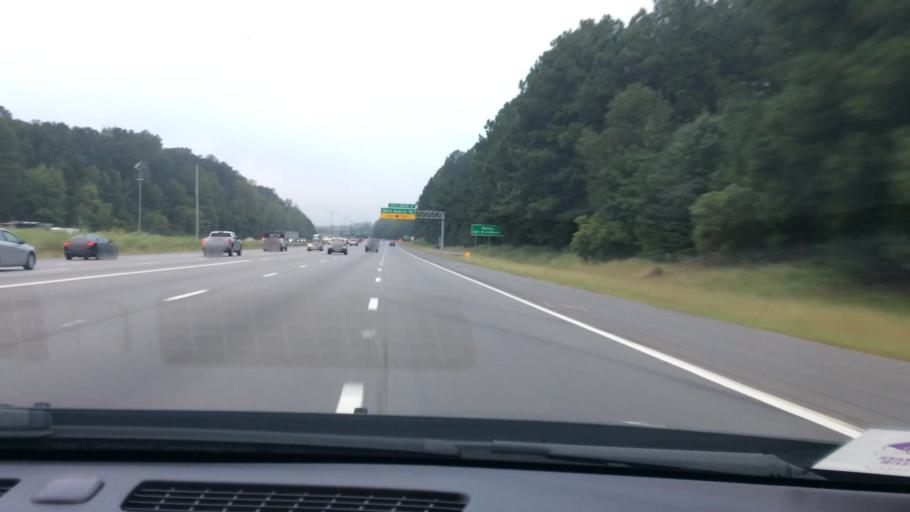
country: US
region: North Carolina
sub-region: Wake County
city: Raleigh
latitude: 35.7561
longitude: -78.5994
